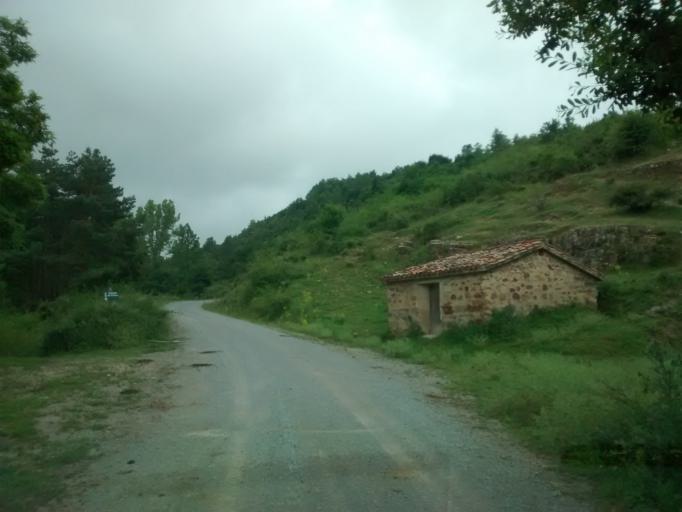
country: ES
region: La Rioja
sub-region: Provincia de La Rioja
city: Ajamil
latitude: 42.1623
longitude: -2.4857
